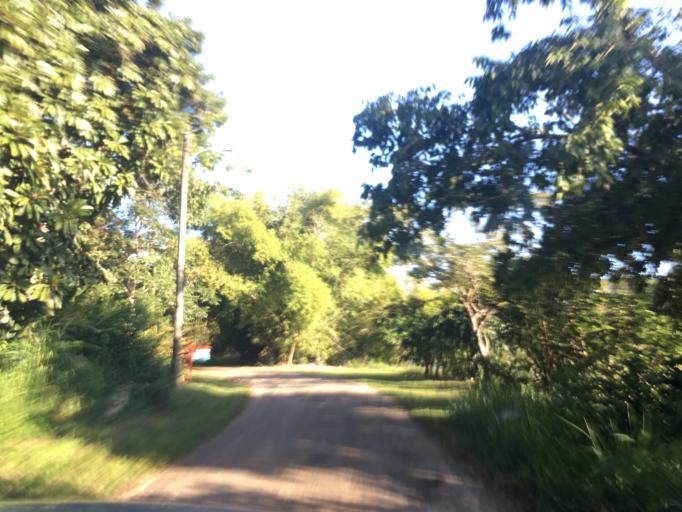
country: BZ
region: Stann Creek
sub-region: Dangriga
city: Dangriga
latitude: 16.8252
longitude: -88.3101
